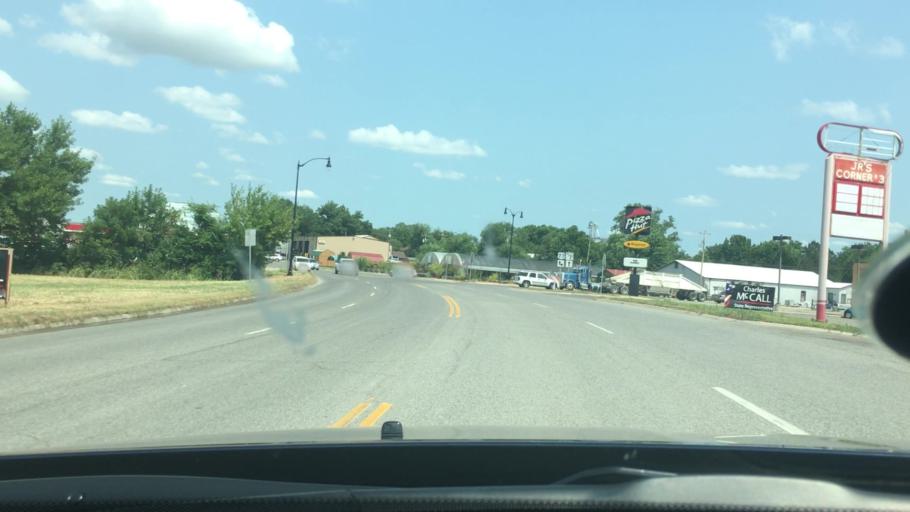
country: US
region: Oklahoma
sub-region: Murray County
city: Davis
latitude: 34.5024
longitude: -97.1274
